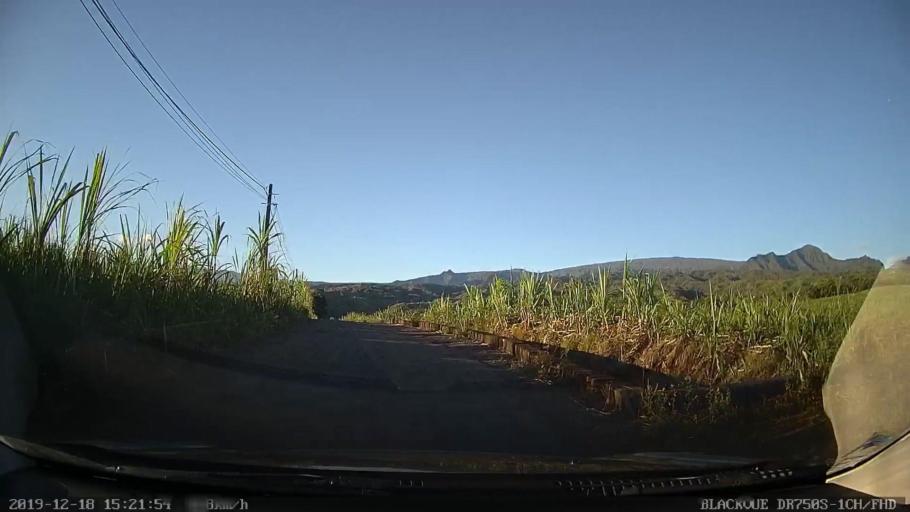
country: RE
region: Reunion
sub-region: Reunion
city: Bras-Panon
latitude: -20.9968
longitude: 55.6625
